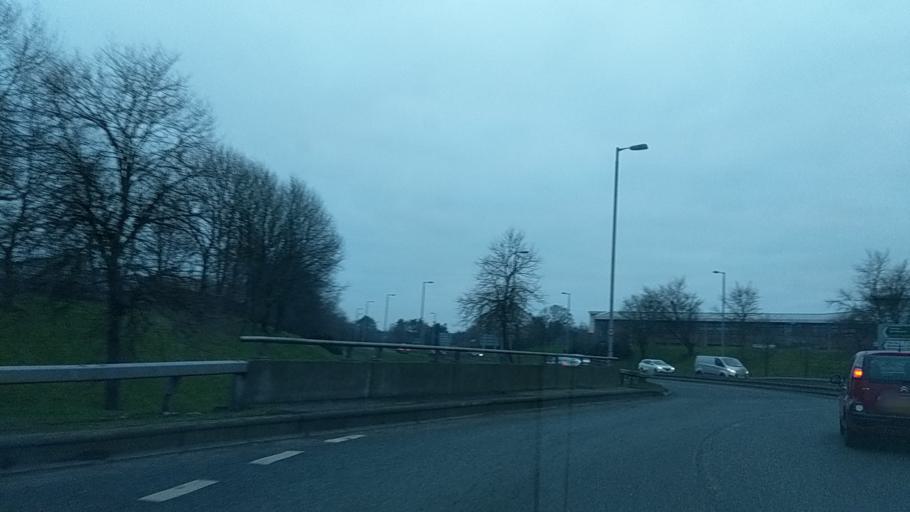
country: GB
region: Scotland
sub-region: South Lanarkshire
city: East Kilbride
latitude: 55.7632
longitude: -4.1651
